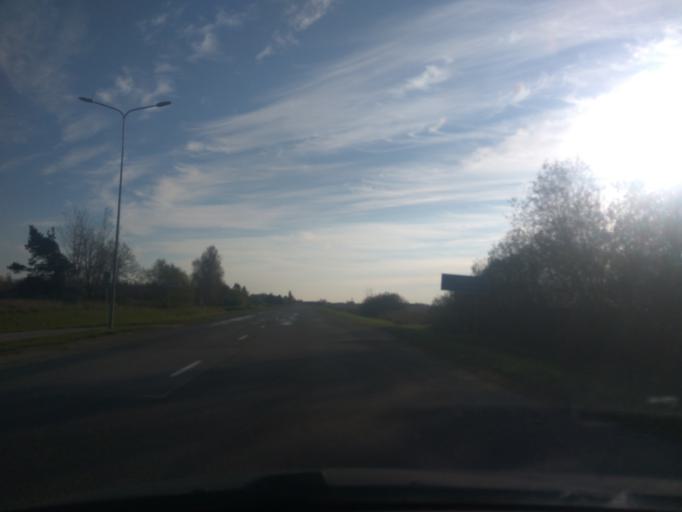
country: LV
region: Ventspils
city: Ventspils
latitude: 57.3545
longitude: 21.5640
